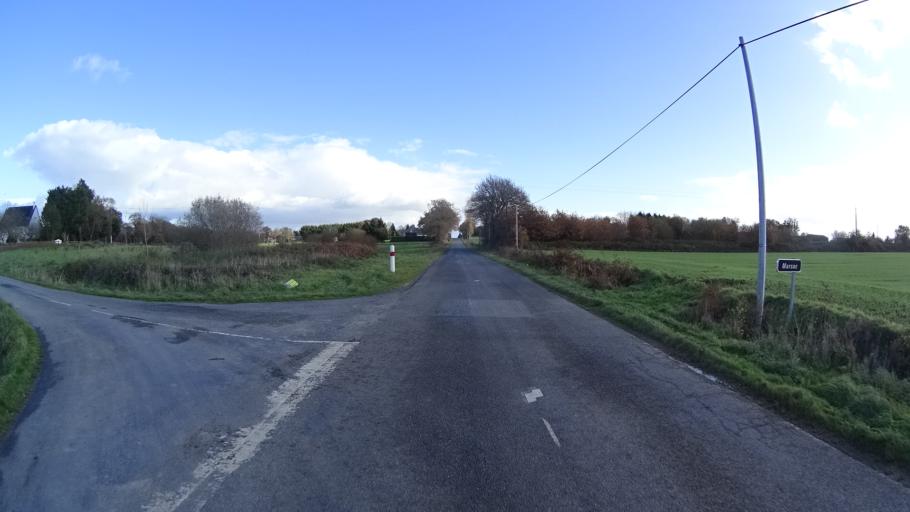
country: FR
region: Brittany
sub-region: Departement du Morbihan
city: Carentoir
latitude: 47.8381
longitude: -2.1149
